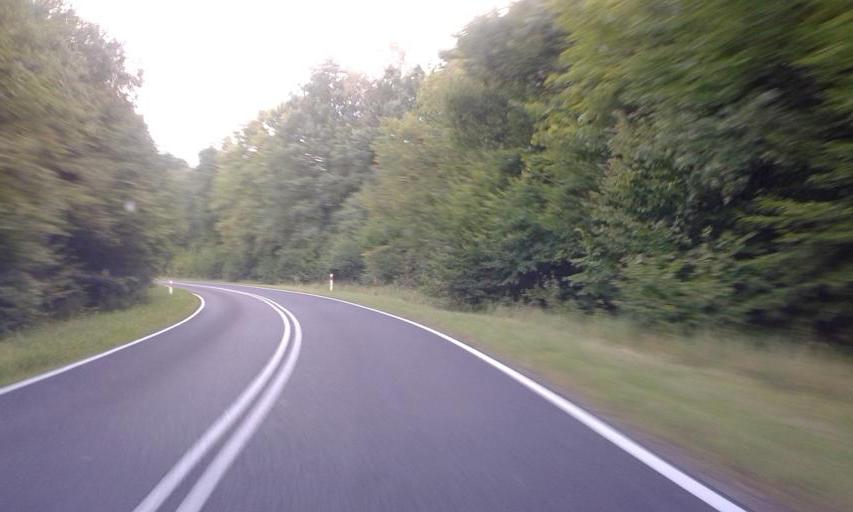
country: PL
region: West Pomeranian Voivodeship
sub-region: Powiat koszalinski
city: Polanow
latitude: 54.0161
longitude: 16.7228
